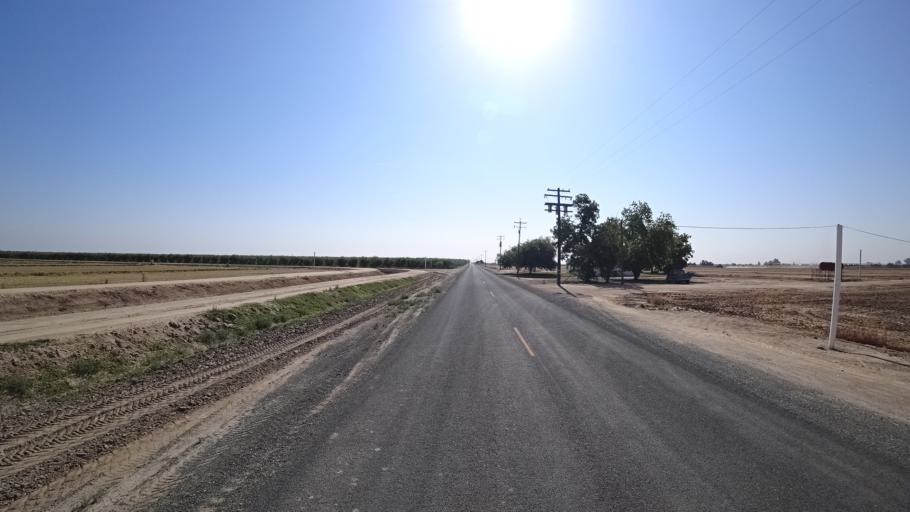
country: US
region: California
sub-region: Kings County
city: Home Garden
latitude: 36.2404
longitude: -119.6149
